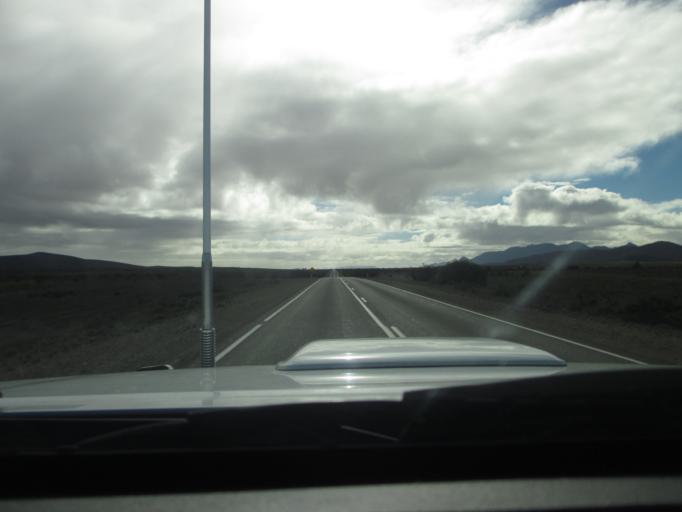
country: AU
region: South Australia
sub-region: Flinders Ranges
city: Quorn
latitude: -31.6500
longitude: 138.3801
